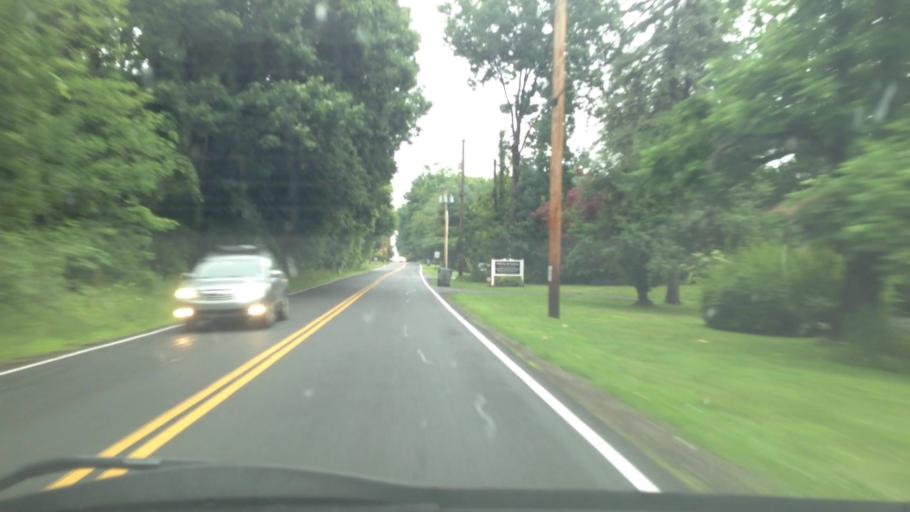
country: US
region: New York
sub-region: Ulster County
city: New Paltz
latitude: 41.7510
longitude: -74.0626
